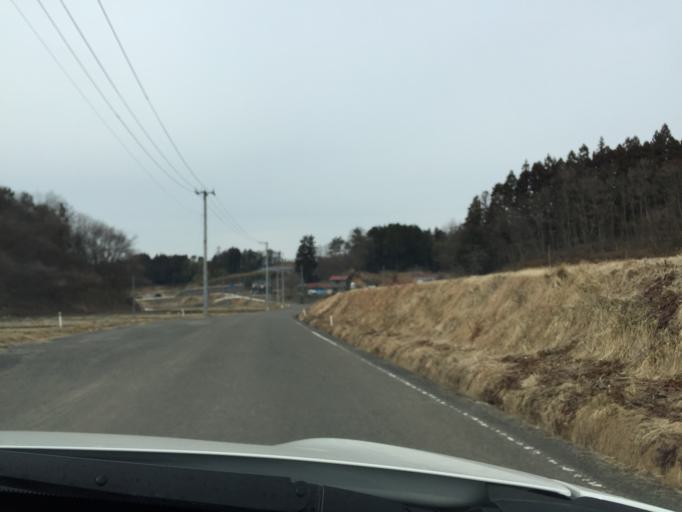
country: JP
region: Fukushima
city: Ishikawa
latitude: 37.2017
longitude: 140.5659
